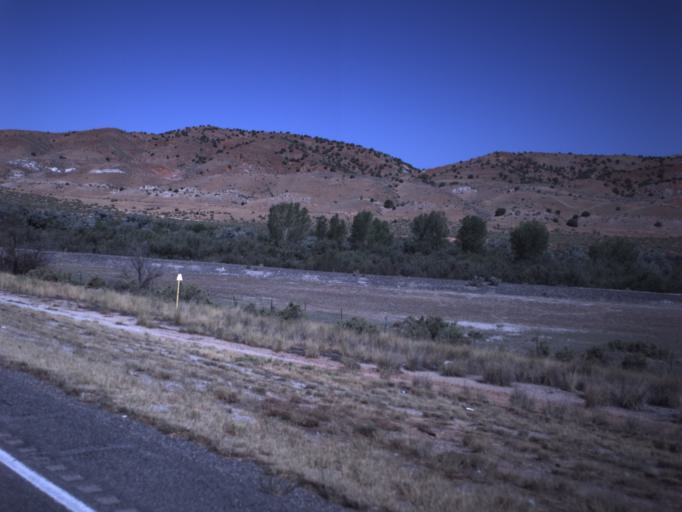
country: US
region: Utah
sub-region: Sanpete County
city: Gunnison
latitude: 39.1678
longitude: -111.7246
